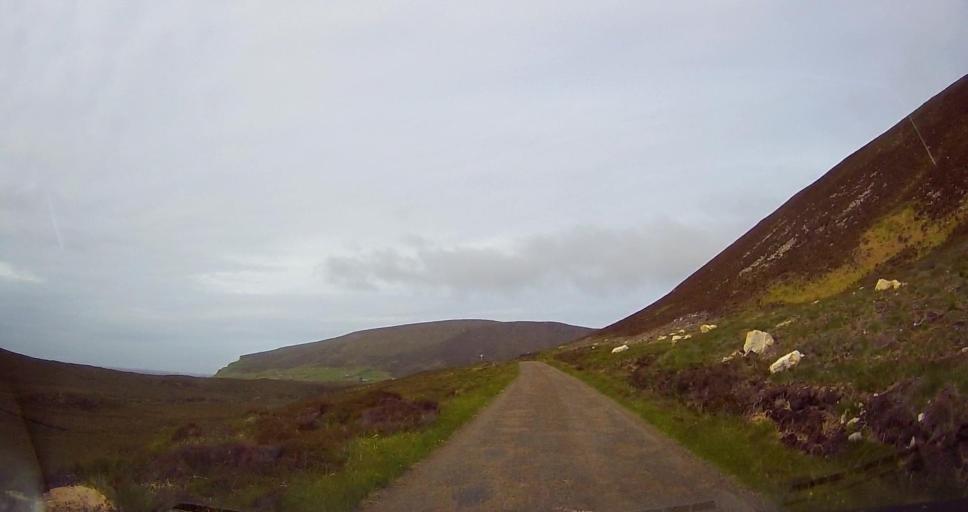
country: GB
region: Scotland
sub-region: Orkney Islands
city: Stromness
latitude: 58.8821
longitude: -3.3582
